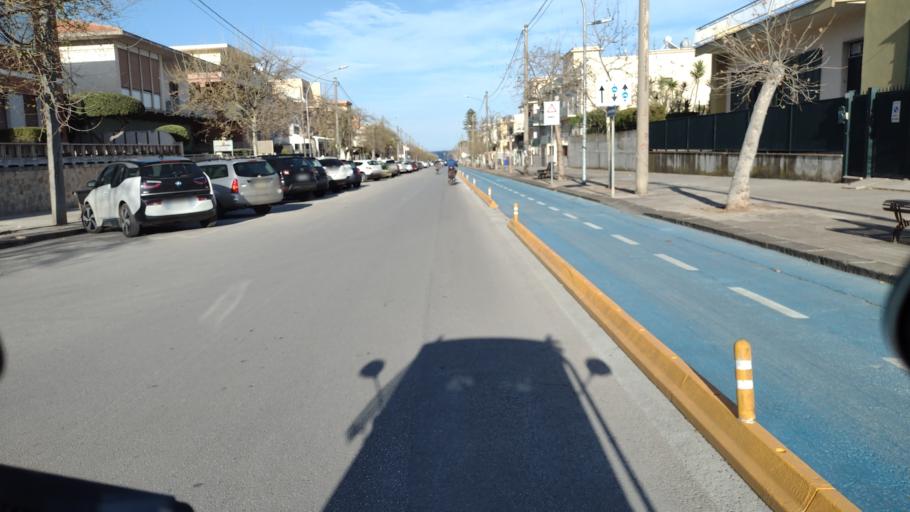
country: IT
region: Sicily
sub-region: Provincia di Siracusa
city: Avola
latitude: 36.9115
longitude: 15.1434
